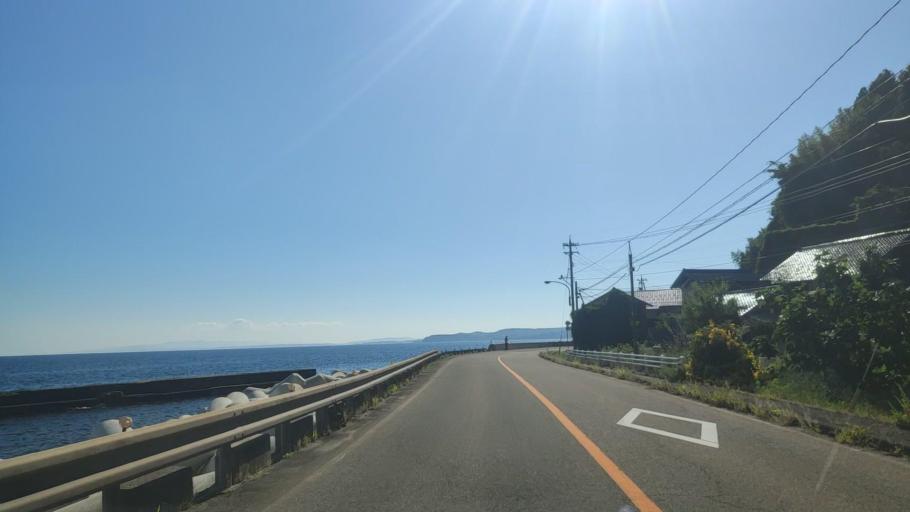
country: JP
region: Ishikawa
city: Nanao
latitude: 37.2913
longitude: 137.1279
